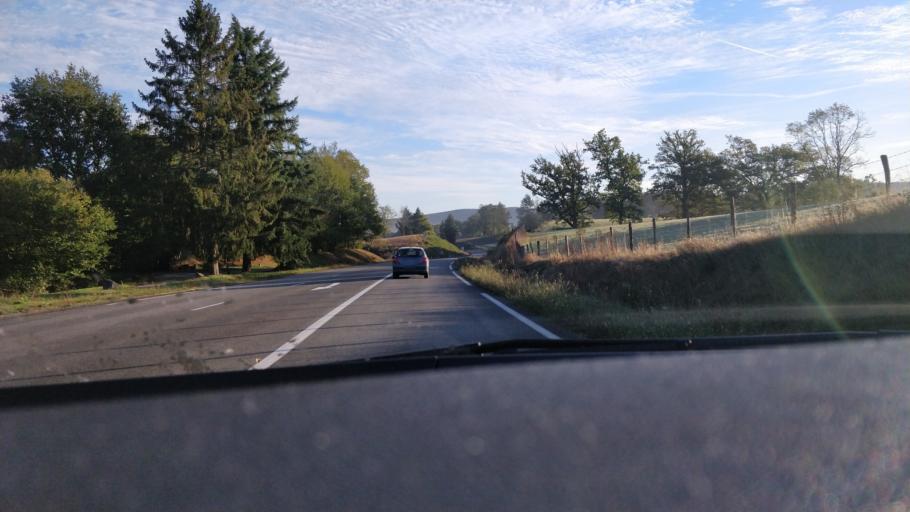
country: FR
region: Limousin
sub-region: Departement de la Creuse
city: Bourganeuf
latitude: 45.9541
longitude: 1.7300
